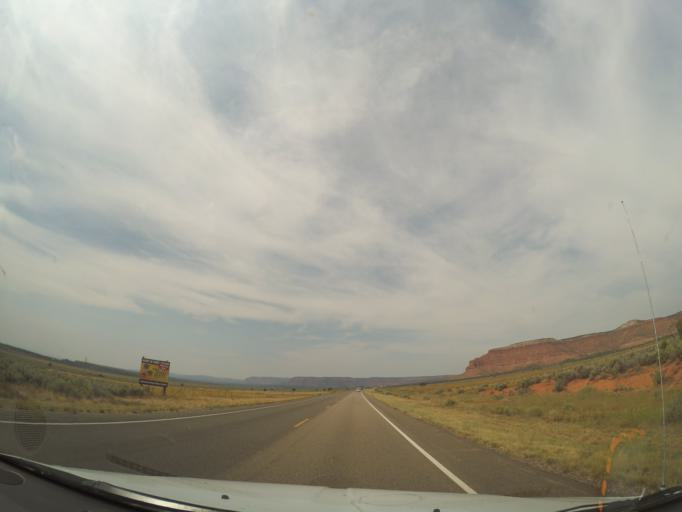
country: US
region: Utah
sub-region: Kane County
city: Kanab
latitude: 37.0234
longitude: -112.4504
